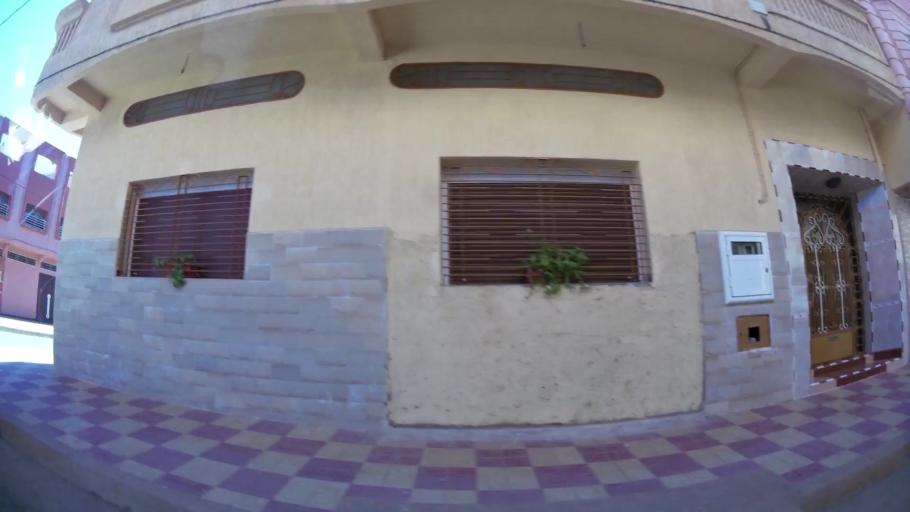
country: MA
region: Oriental
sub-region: Berkane-Taourirt
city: Berkane
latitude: 34.9381
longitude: -2.3354
